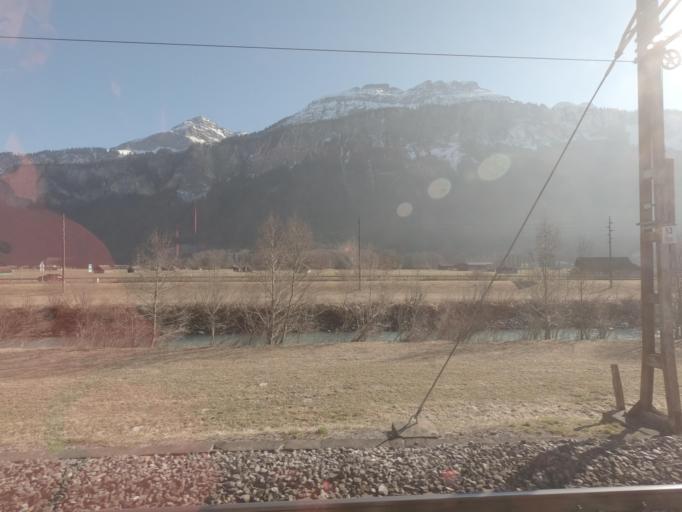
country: CH
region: Bern
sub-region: Interlaken-Oberhasli District
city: Brienz
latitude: 46.7450
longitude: 8.0862
